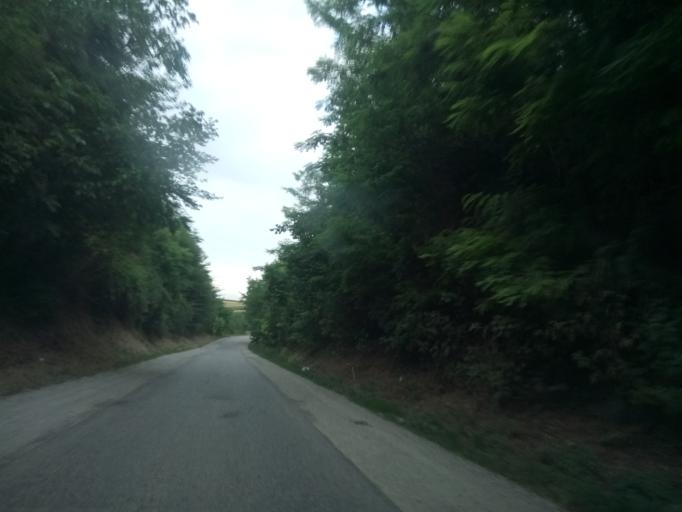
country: RS
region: Autonomna Pokrajina Vojvodina
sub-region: Sremski Okrug
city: Irig
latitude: 45.0993
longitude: 19.8878
